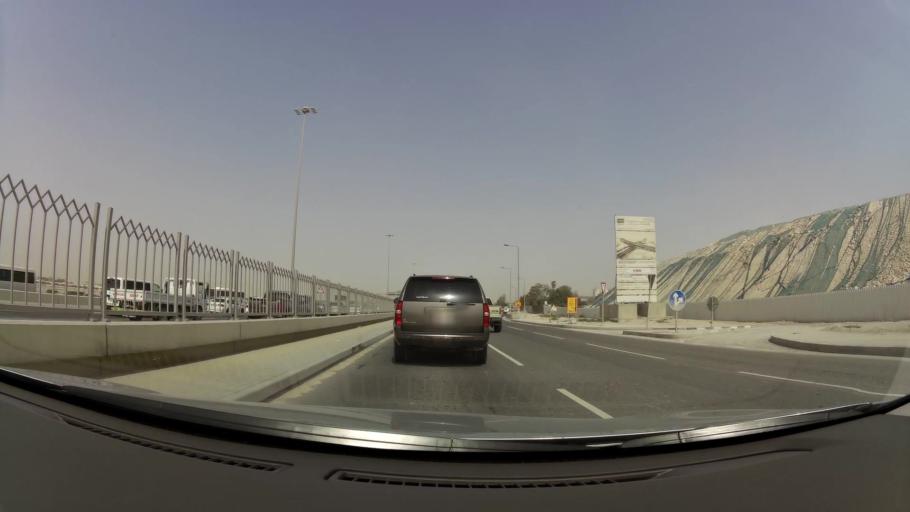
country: QA
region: Baladiyat ad Dawhah
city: Doha
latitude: 25.2885
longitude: 51.4799
